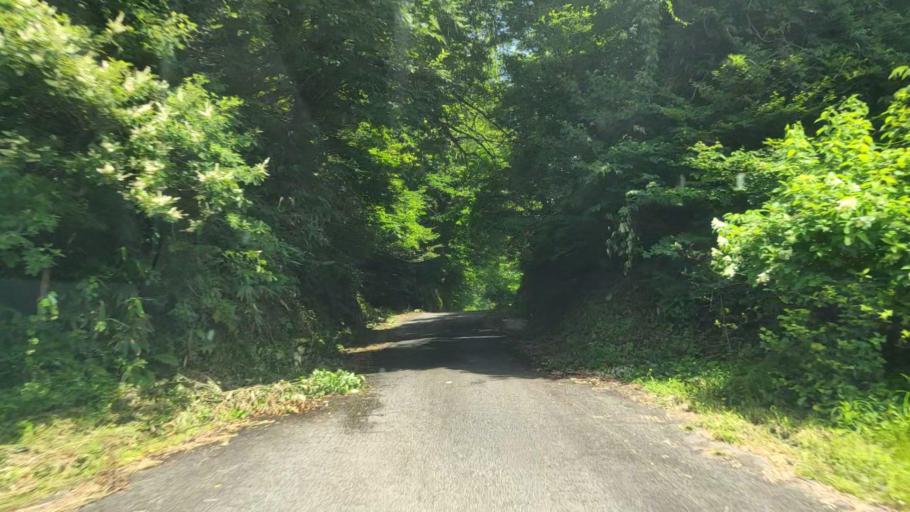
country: JP
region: Fukui
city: Ono
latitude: 35.7974
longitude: 136.4919
